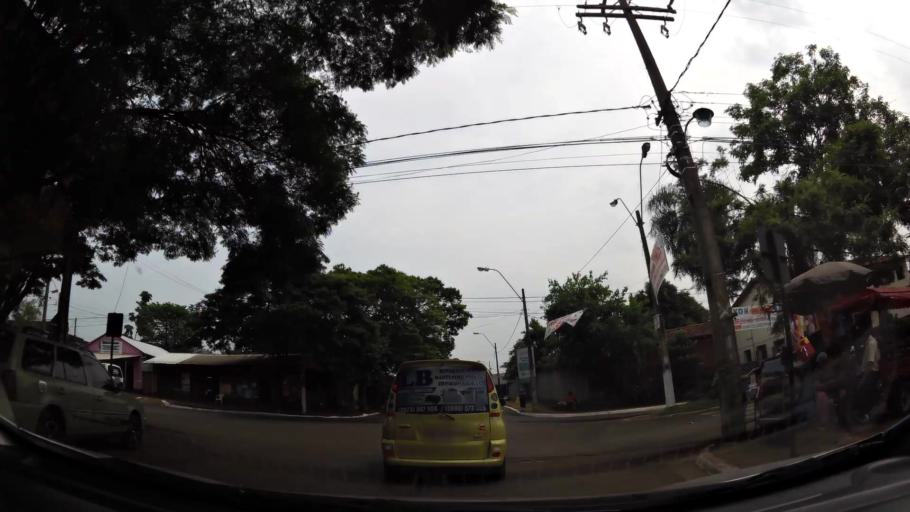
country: BR
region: Parana
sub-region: Foz Do Iguacu
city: Foz do Iguacu
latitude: -25.5584
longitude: -54.6047
